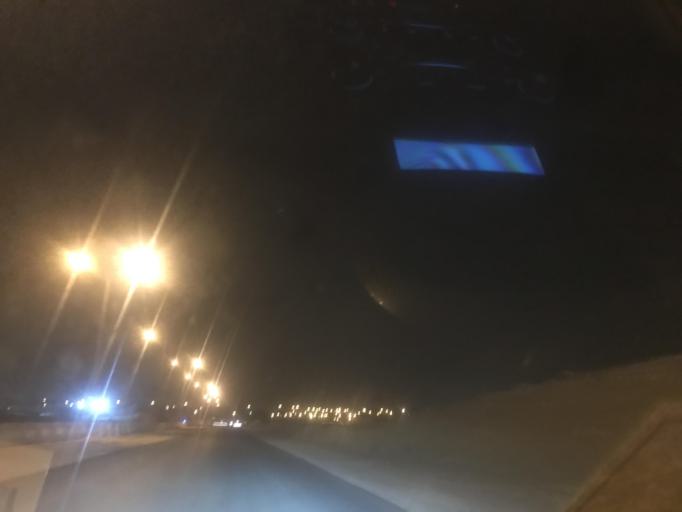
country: SA
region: Ar Riyad
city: Riyadh
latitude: 24.7606
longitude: 46.5890
